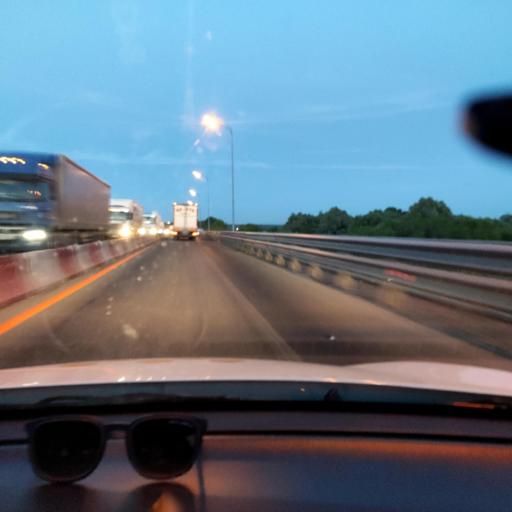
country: RU
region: Tatarstan
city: Pestretsy
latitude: 55.7010
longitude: 49.5768
